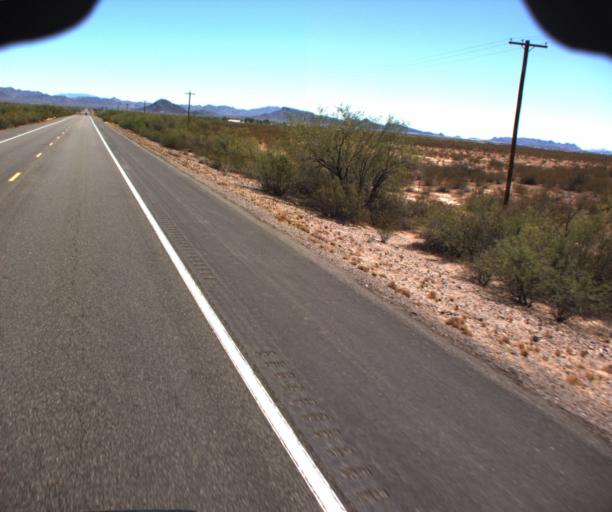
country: US
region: Arizona
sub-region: La Paz County
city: Salome
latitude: 33.7059
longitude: -113.8301
